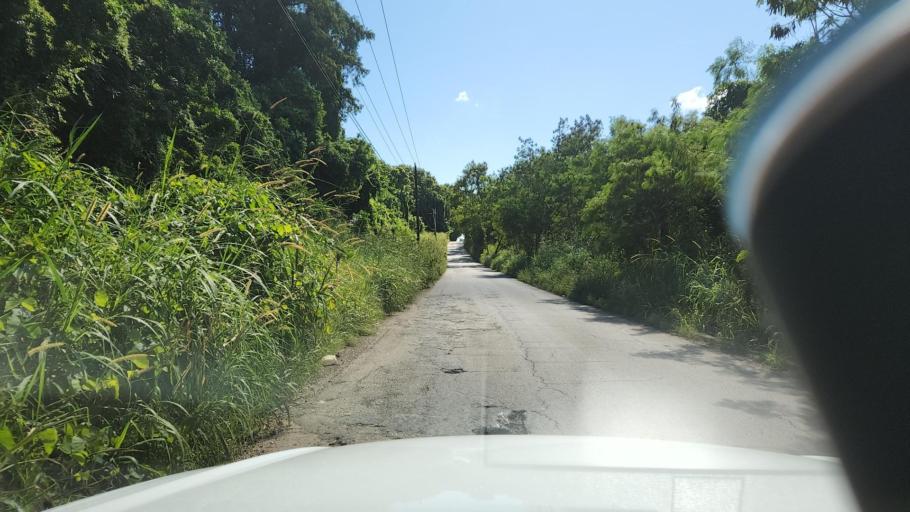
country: BB
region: Saint Thomas
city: Welchman Hall
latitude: 13.1845
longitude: -59.5970
